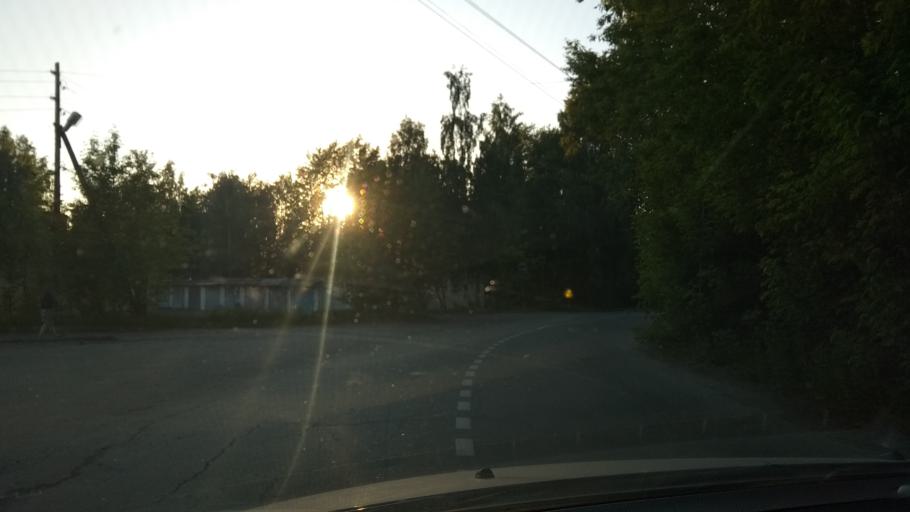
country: RU
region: Sverdlovsk
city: Sredneuralsk
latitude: 56.9828
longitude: 60.4602
